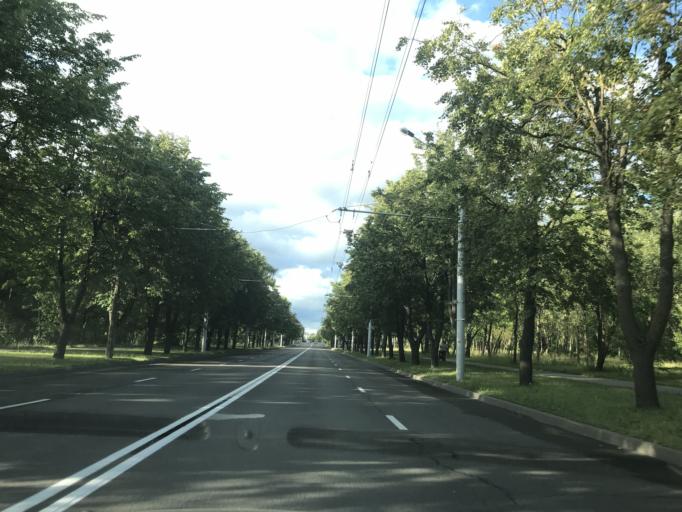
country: BY
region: Minsk
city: Minsk
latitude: 53.9413
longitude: 27.6185
